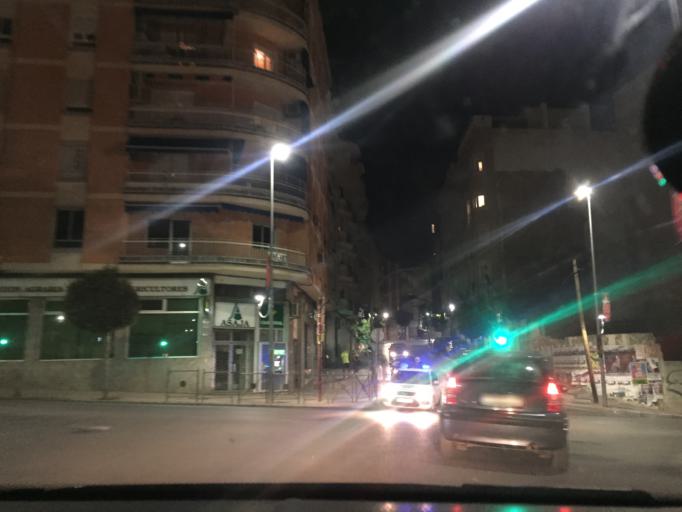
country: ES
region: Andalusia
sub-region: Provincia de Jaen
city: Jaen
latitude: 37.7687
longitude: -3.7833
